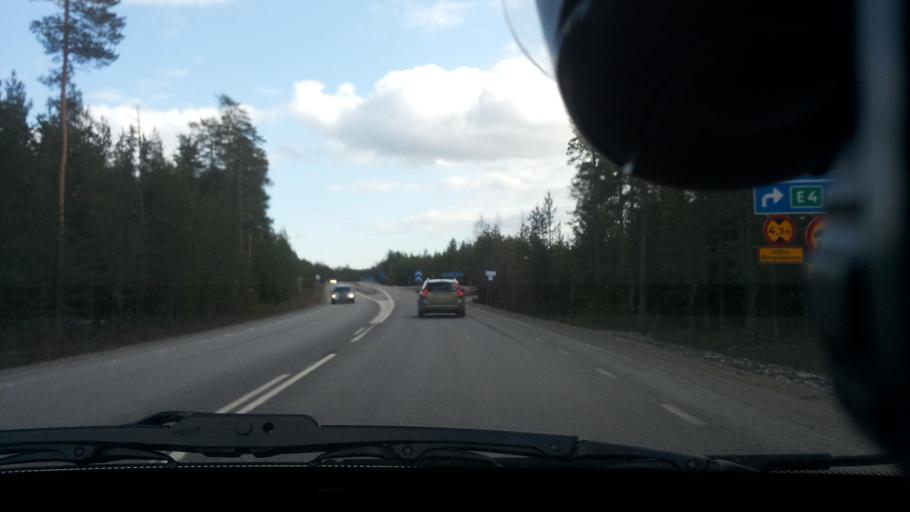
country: SE
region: Norrbotten
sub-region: Lulea Kommun
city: Gammelstad
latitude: 65.6003
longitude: 22.0391
